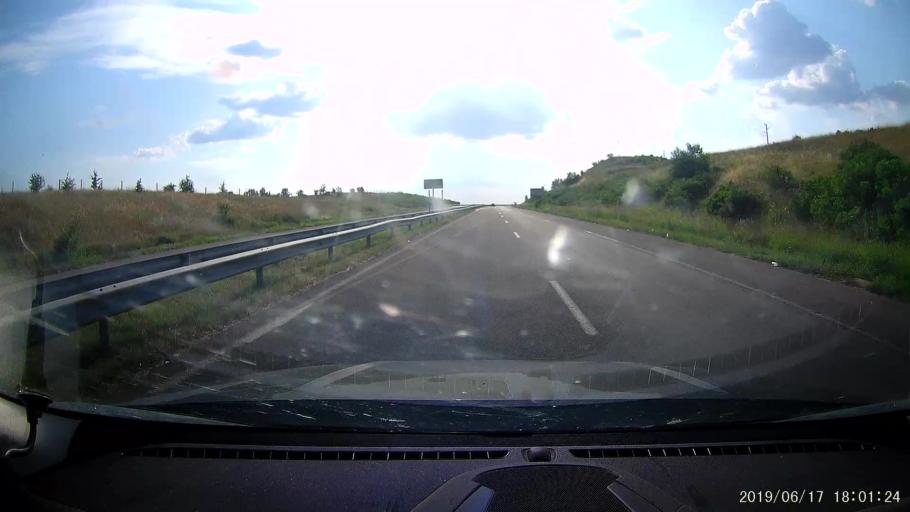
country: BG
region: Khaskovo
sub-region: Obshtina Svilengrad
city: Svilengrad
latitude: 41.7456
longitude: 26.2555
